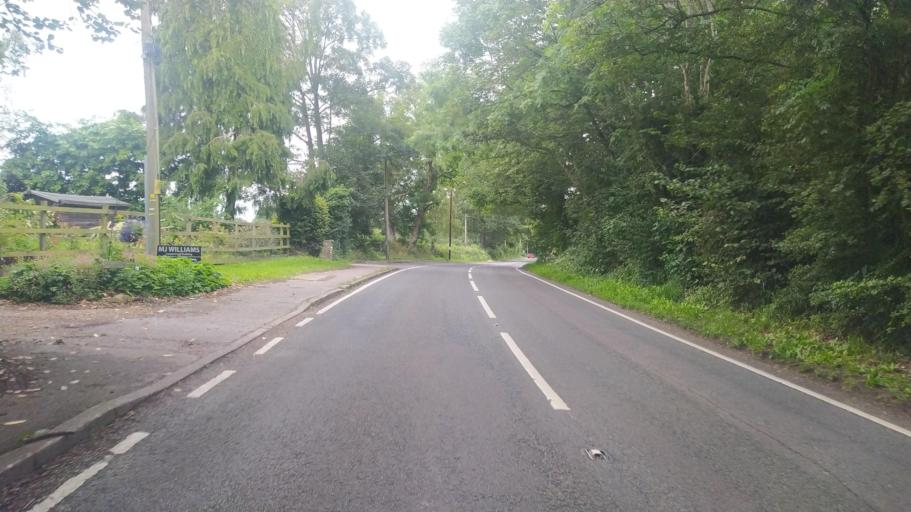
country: GB
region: England
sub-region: Hampshire
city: Liphook
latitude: 51.0896
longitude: -0.8156
